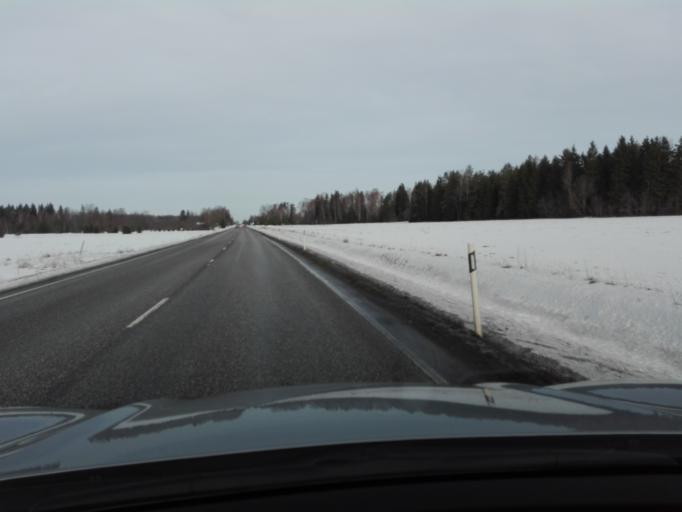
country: EE
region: Raplamaa
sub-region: Rapla vald
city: Rapla
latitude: 58.9797
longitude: 24.7822
